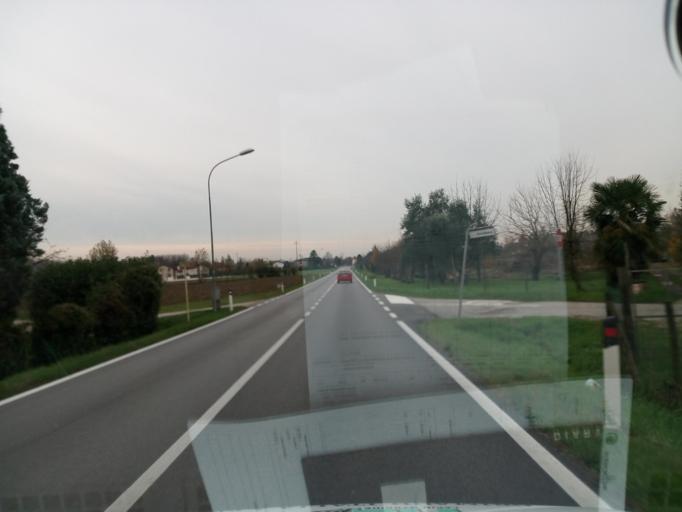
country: IT
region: Veneto
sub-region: Provincia di Padova
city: Piombino Dese
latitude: 45.5900
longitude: 12.0016
